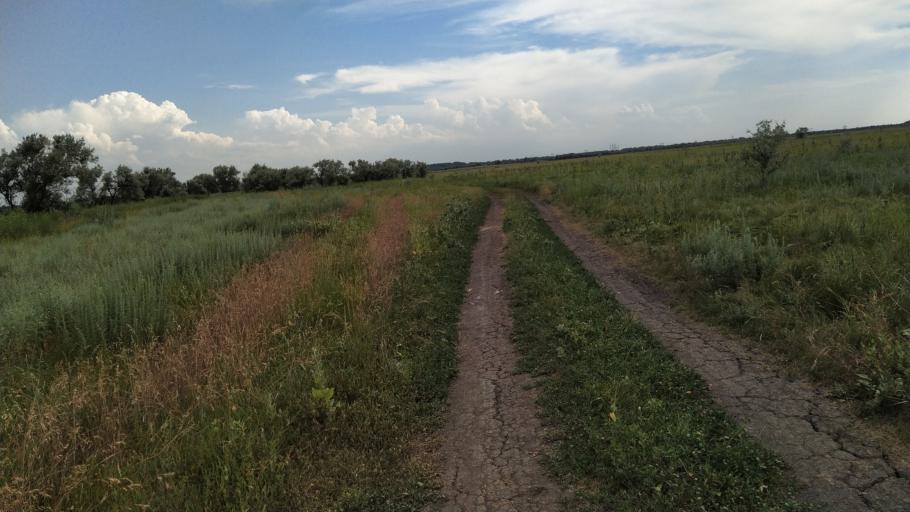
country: RU
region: Rostov
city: Kuleshovka
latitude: 47.1319
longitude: 39.6298
